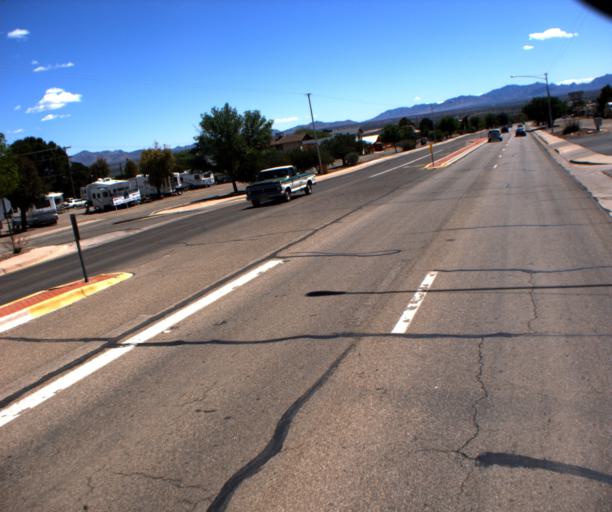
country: US
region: Arizona
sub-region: Cochise County
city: Benson
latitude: 31.9708
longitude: -110.3121
